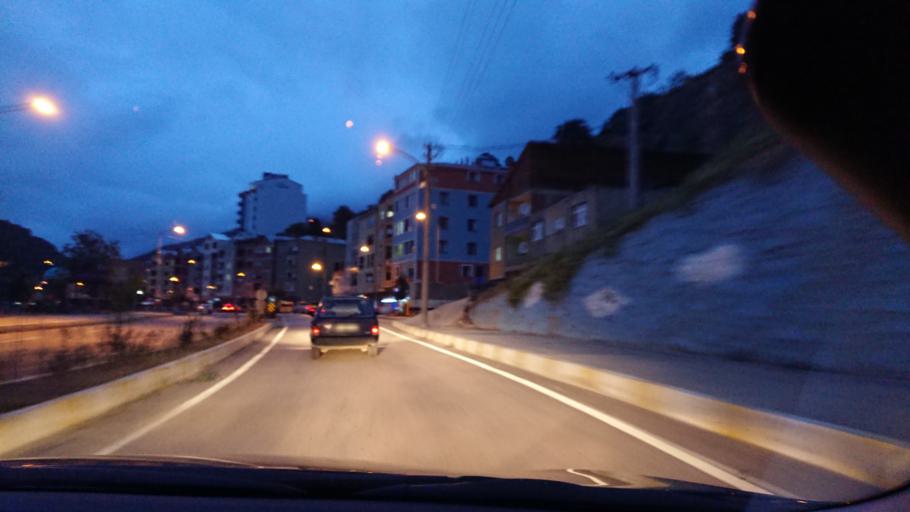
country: TR
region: Gumushane
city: Kurtun
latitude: 40.6676
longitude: 39.1418
